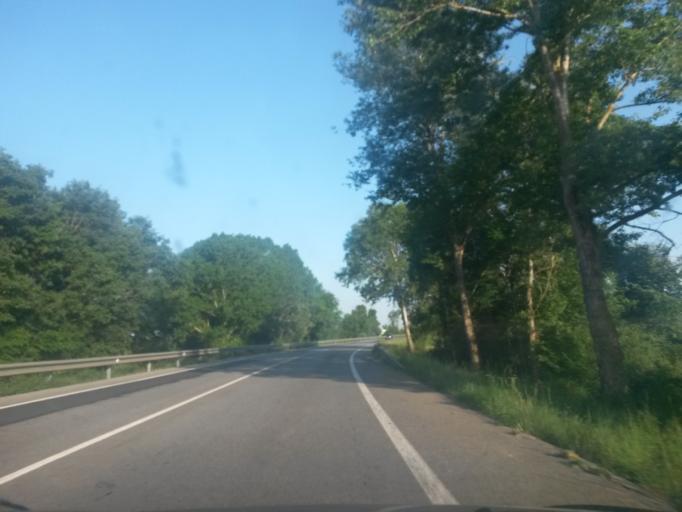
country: ES
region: Catalonia
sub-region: Provincia de Girona
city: Banyoles
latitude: 42.1521
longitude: 2.7601
